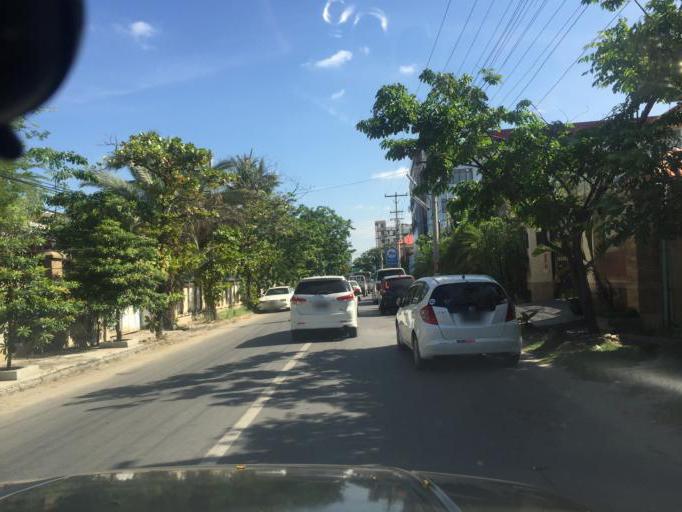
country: MM
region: Mandalay
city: Mandalay
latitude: 21.9520
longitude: 96.1082
